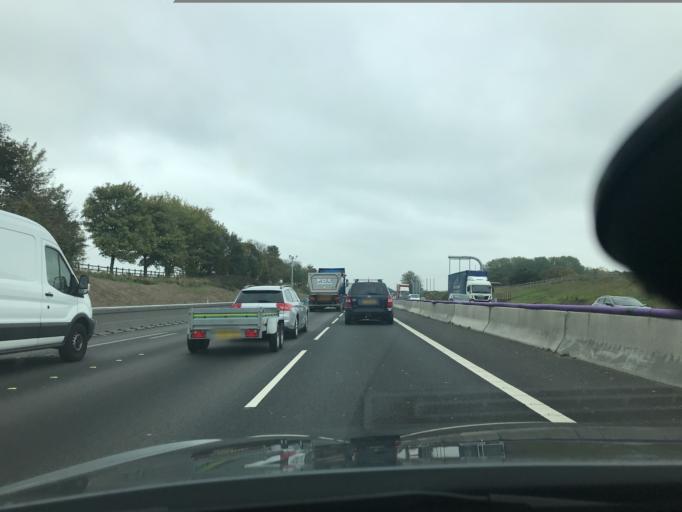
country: GB
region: England
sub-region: Cheshire East
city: Knutsford
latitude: 53.2941
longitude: -2.3975
